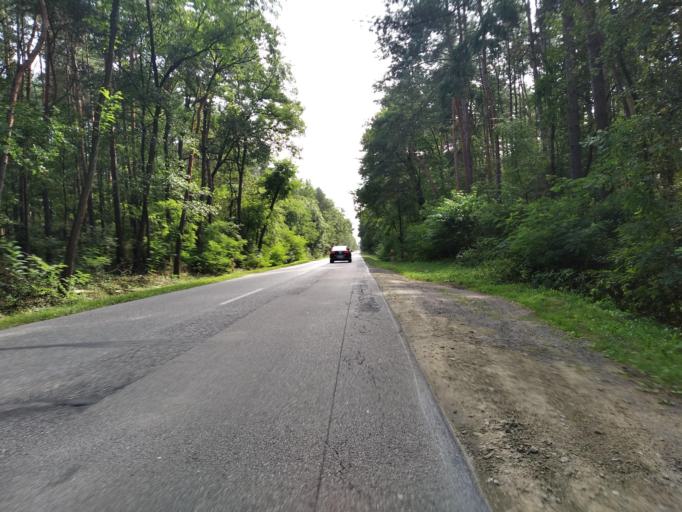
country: PL
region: Subcarpathian Voivodeship
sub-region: Powiat ropczycko-sedziszowski
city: Ostrow
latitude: 50.1492
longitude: 21.5708
